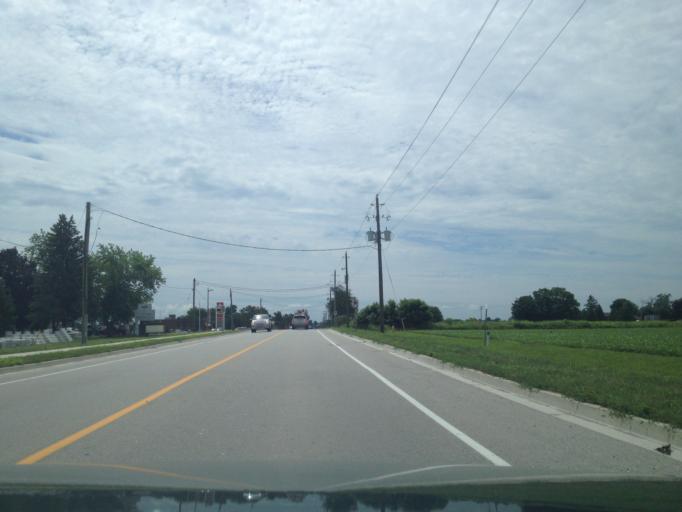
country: CA
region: Ontario
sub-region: Oxford County
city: Woodstock
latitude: 42.9762
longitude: -80.5944
